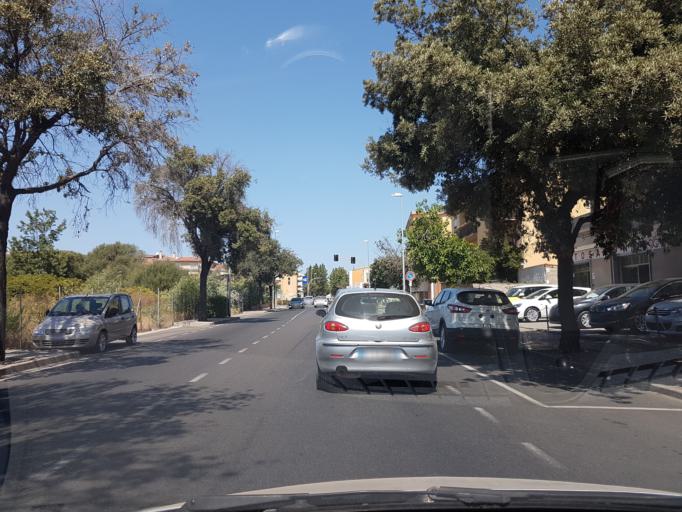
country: IT
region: Sardinia
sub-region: Provincia di Oristano
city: Oristano
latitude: 39.8949
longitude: 8.5967
